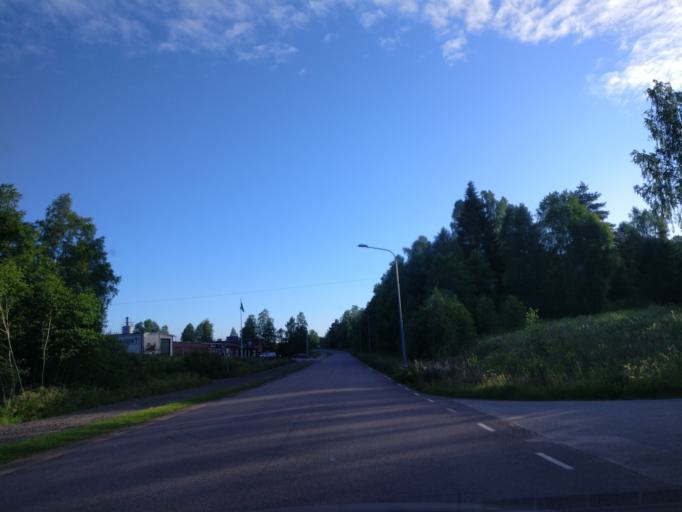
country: SE
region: Vaermland
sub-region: Hagfors Kommun
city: Hagfors
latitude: 60.0218
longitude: 13.6927
